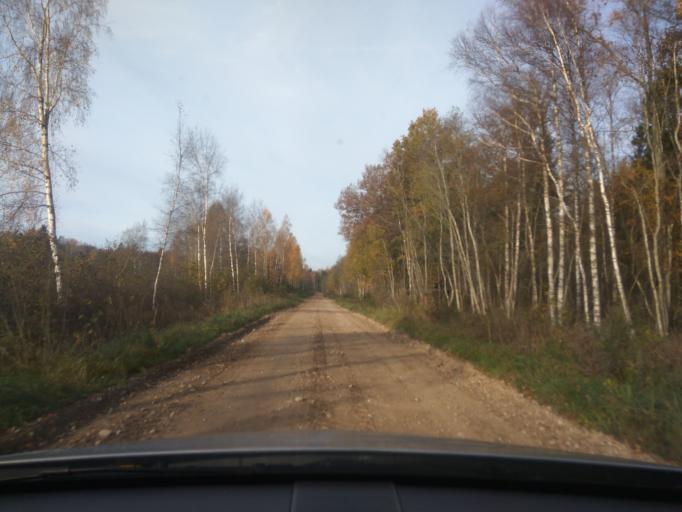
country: LV
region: Aizpute
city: Aizpute
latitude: 56.8398
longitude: 21.7250
